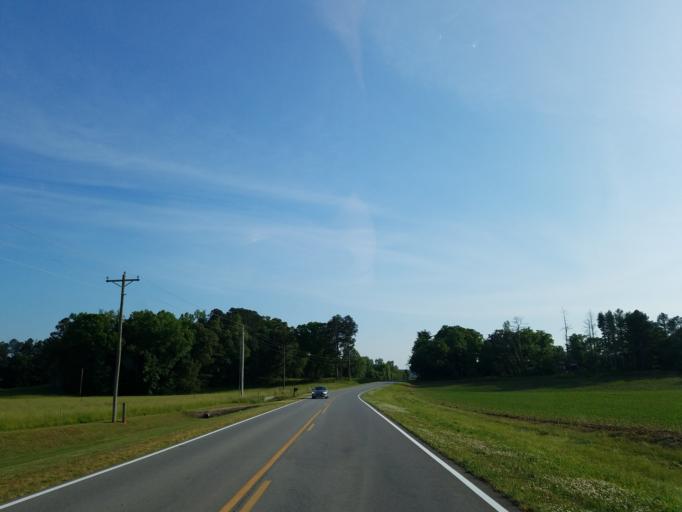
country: US
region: Georgia
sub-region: Chattooga County
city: Trion
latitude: 34.4743
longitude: -85.2637
